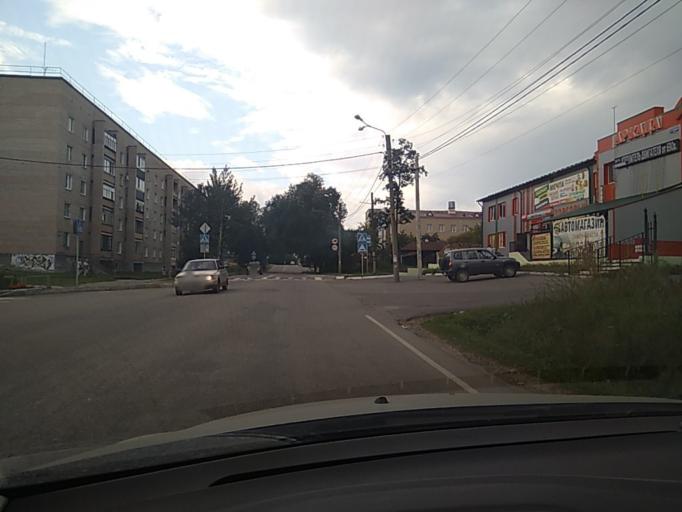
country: RU
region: Chelyabinsk
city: Kyshtym
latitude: 55.7009
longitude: 60.5530
